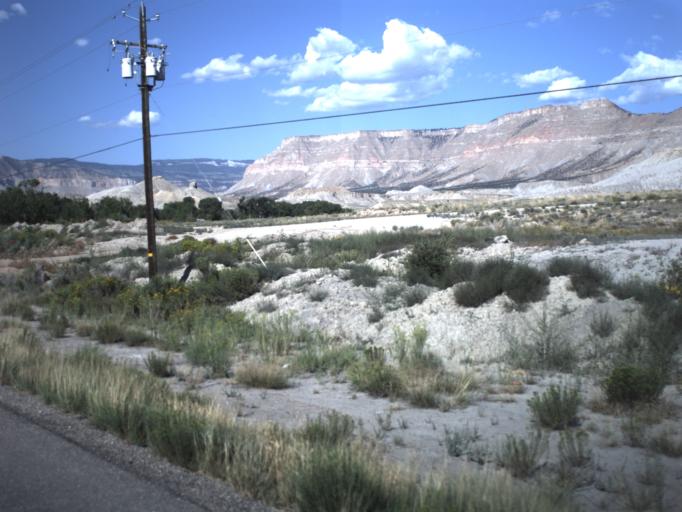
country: US
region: Utah
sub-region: Emery County
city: Ferron
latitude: 39.1245
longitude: -111.1097
